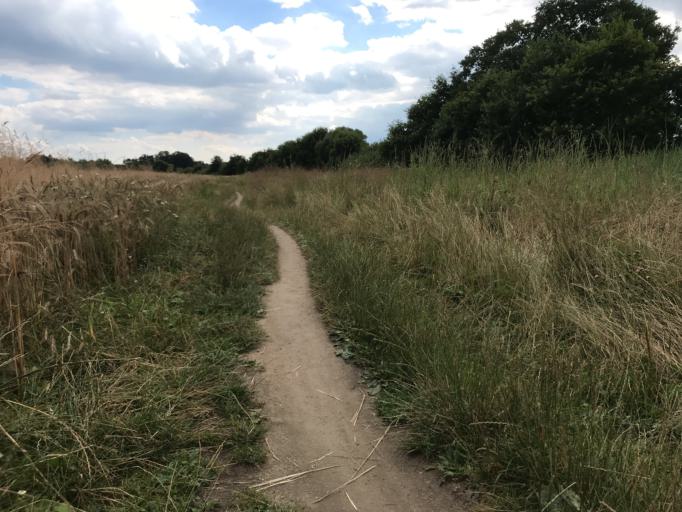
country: CZ
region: Jihocesky
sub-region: Okres Jindrichuv Hradec
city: Trebon
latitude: 48.9912
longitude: 14.7527
